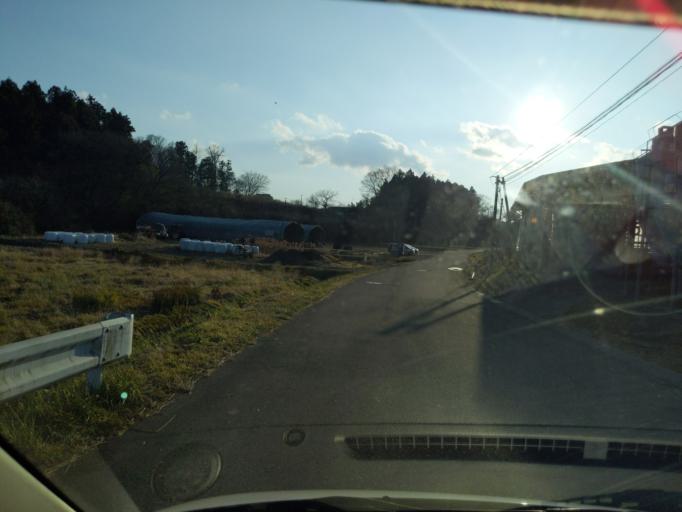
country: JP
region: Miyagi
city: Wakuya
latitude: 38.6980
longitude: 141.1104
